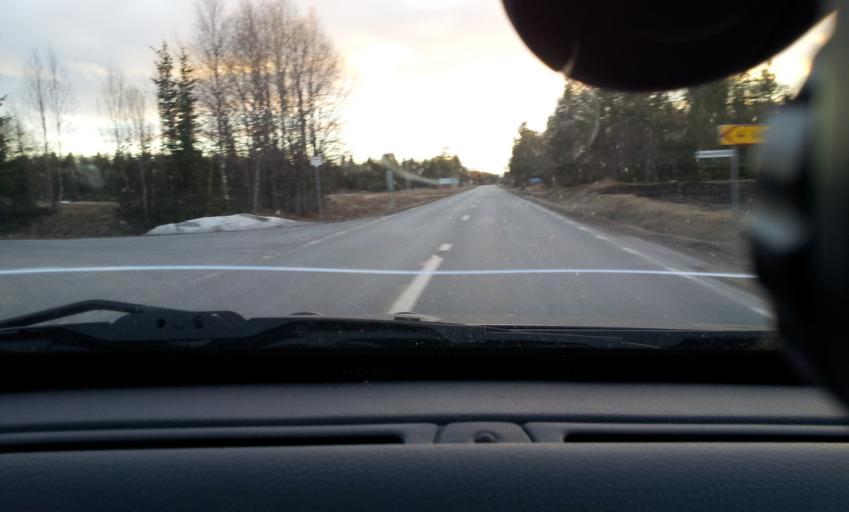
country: SE
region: Jaemtland
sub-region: Bergs Kommun
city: Hoverberg
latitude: 62.9694
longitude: 14.5571
